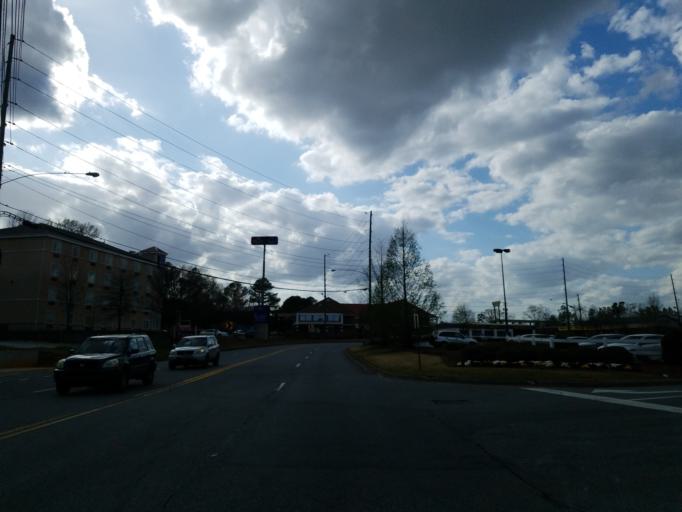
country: US
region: Georgia
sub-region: Cobb County
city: Kennesaw
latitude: 34.0551
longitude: -84.5909
